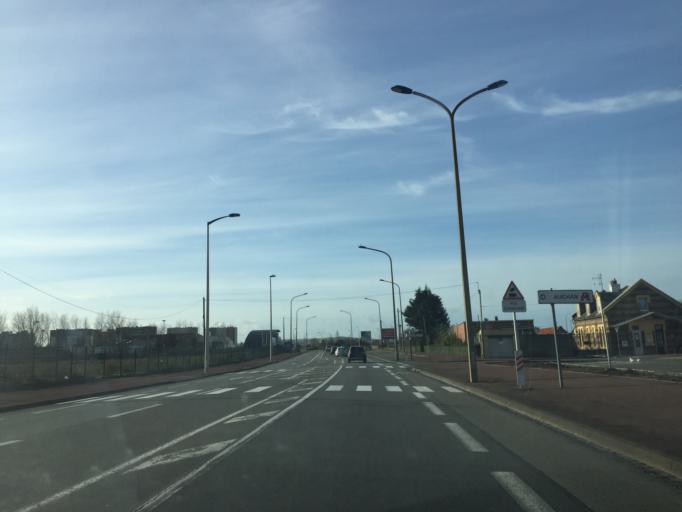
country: FR
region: Nord-Pas-de-Calais
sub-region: Departement du Pas-de-Calais
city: Calais
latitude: 50.9530
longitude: 1.8358
